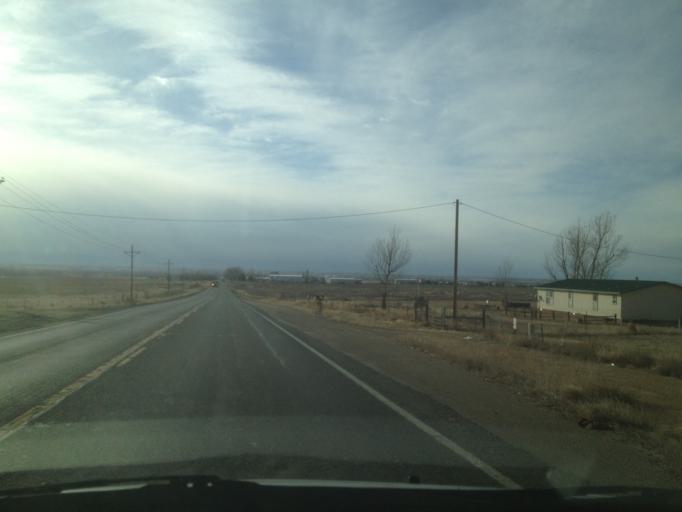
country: US
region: Colorado
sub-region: Weld County
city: Aristocrat Ranchettes
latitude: 40.0804
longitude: -104.7539
